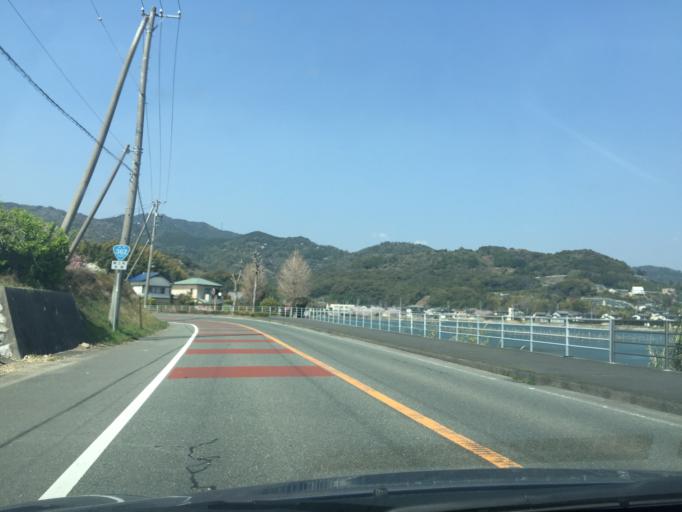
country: JP
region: Shizuoka
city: Kosai-shi
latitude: 34.7973
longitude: 137.6202
